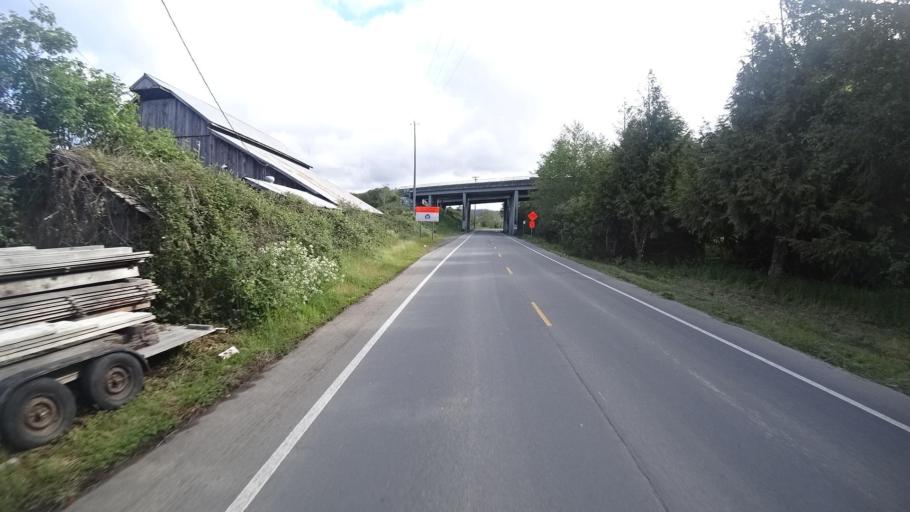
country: US
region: California
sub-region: Humboldt County
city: Arcata
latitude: 40.8912
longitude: -124.0814
